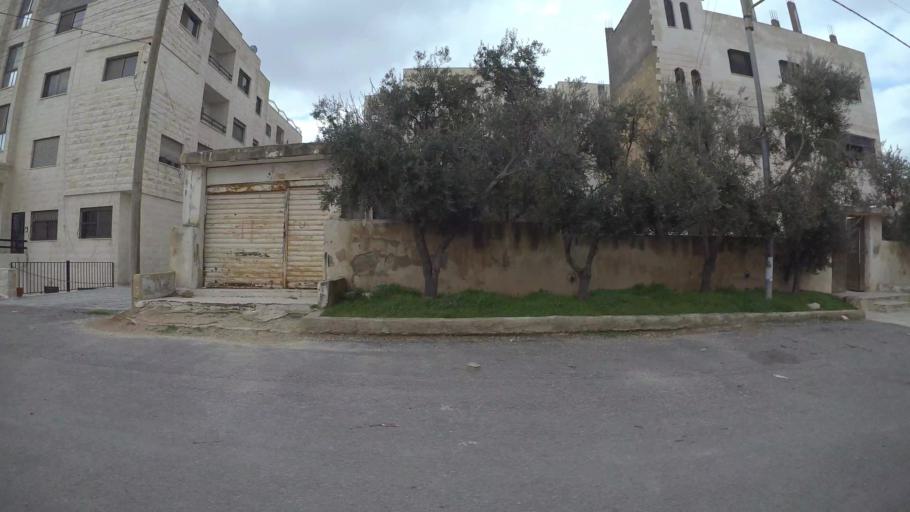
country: JO
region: Amman
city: Al Jubayhah
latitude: 32.0373
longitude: 35.8258
